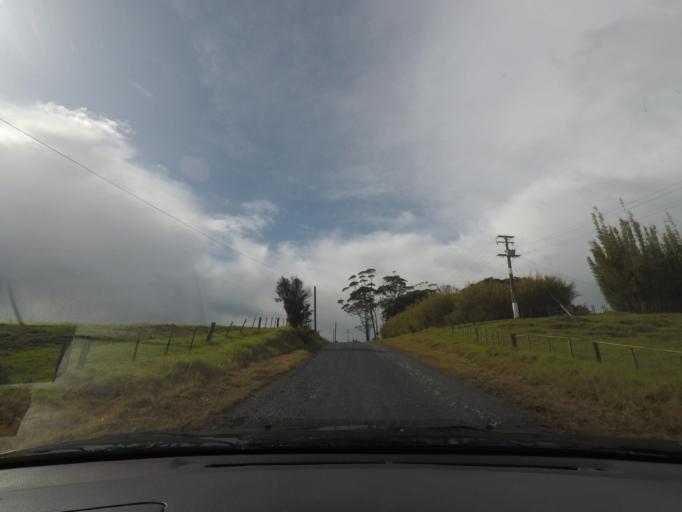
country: NZ
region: Auckland
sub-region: Auckland
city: Warkworth
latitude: -36.4317
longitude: 174.7193
